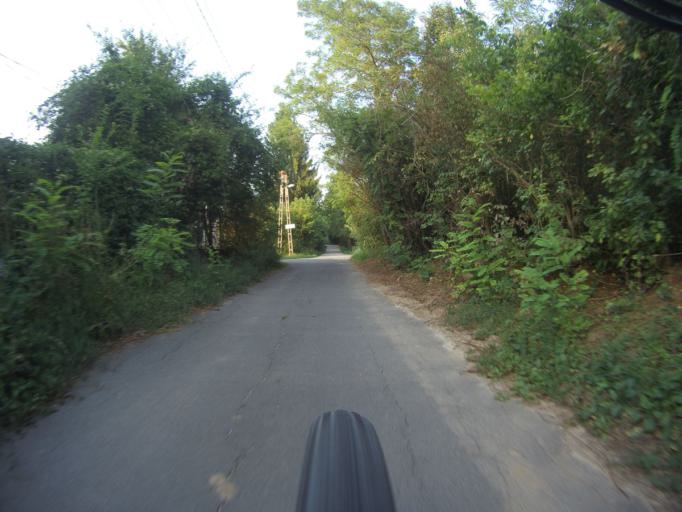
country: HU
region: Pest
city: Budakeszi
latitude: 47.5481
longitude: 18.9692
